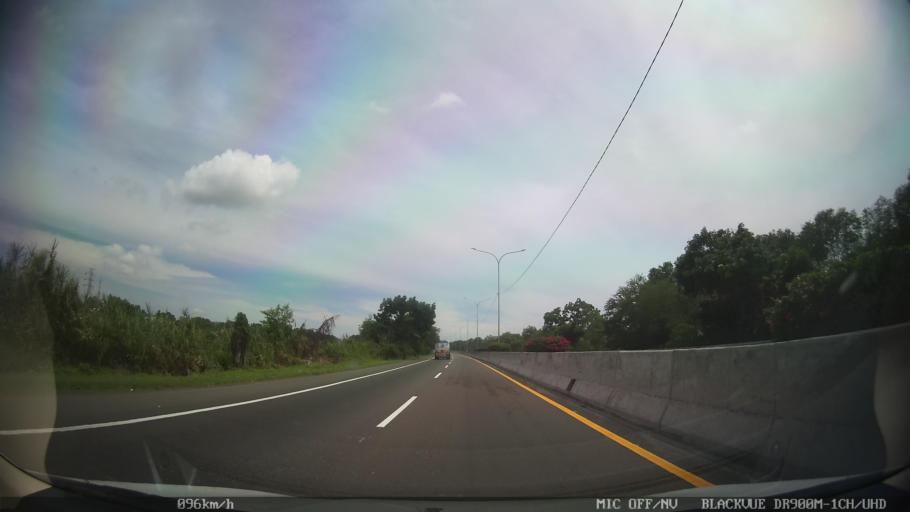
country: ID
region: North Sumatra
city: Labuhan Deli
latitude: 3.7505
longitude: 98.6815
